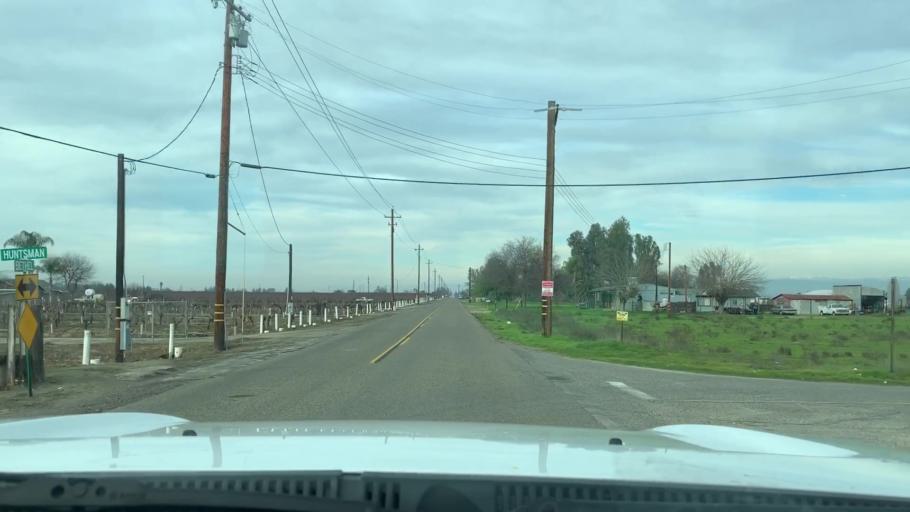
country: US
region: California
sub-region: Fresno County
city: Selma
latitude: 36.5834
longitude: -119.5749
